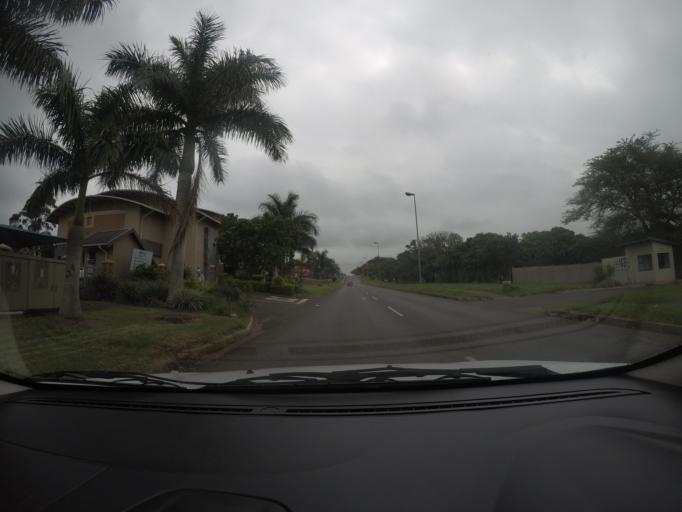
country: ZA
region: KwaZulu-Natal
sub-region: uThungulu District Municipality
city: Empangeni
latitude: -28.7376
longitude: 31.8926
